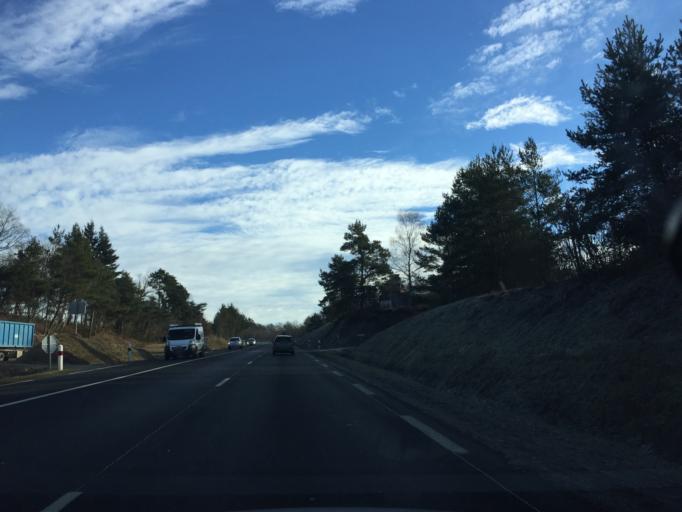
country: FR
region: Auvergne
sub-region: Departement du Puy-de-Dome
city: Gelles
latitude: 45.8543
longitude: 2.6762
